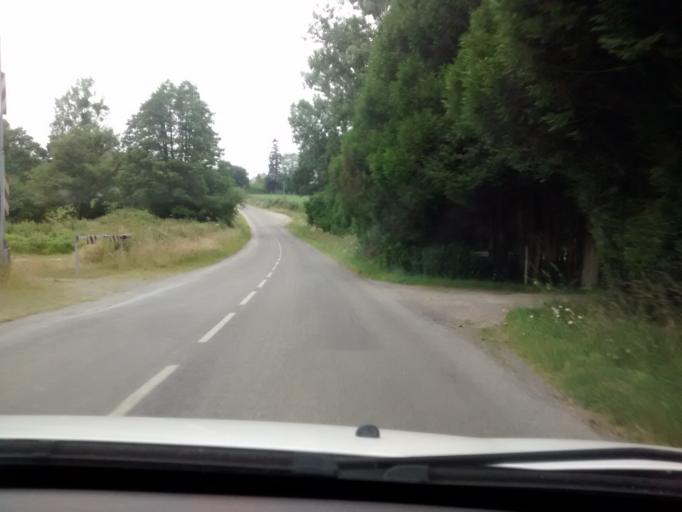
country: FR
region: Brittany
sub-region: Departement d'Ille-et-Vilaine
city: La Bouexiere
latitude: 48.1918
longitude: -1.4519
